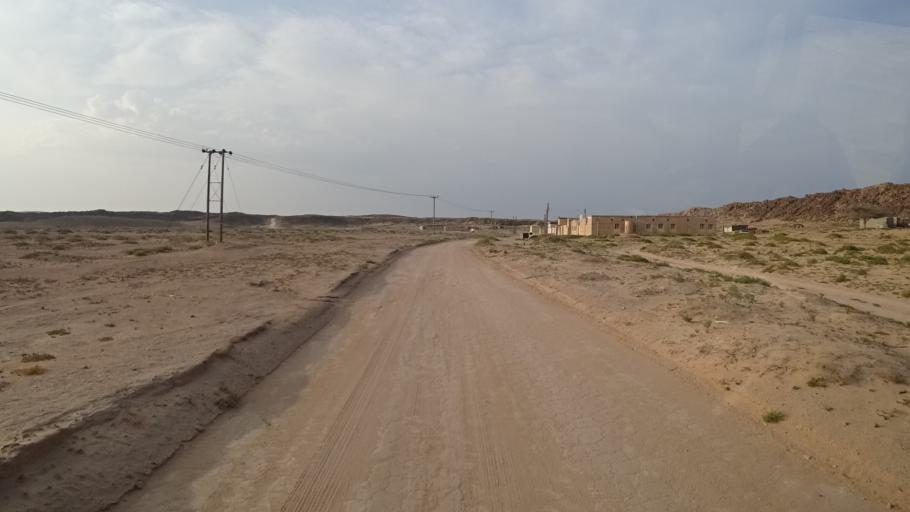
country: OM
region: Ash Sharqiyah
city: Sur
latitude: 22.4465
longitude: 59.8271
